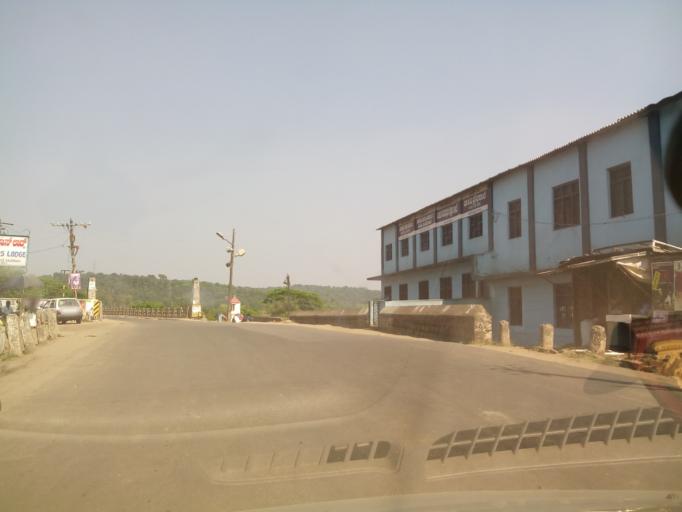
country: IN
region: Karnataka
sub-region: Hassan
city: Sakleshpur
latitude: 12.9445
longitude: 75.7921
